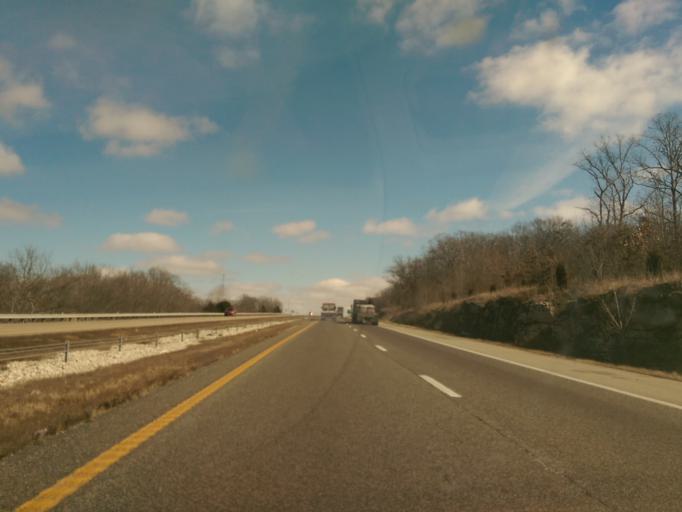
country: US
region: Missouri
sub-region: Montgomery County
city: Montgomery City
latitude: 38.9025
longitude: -91.5666
